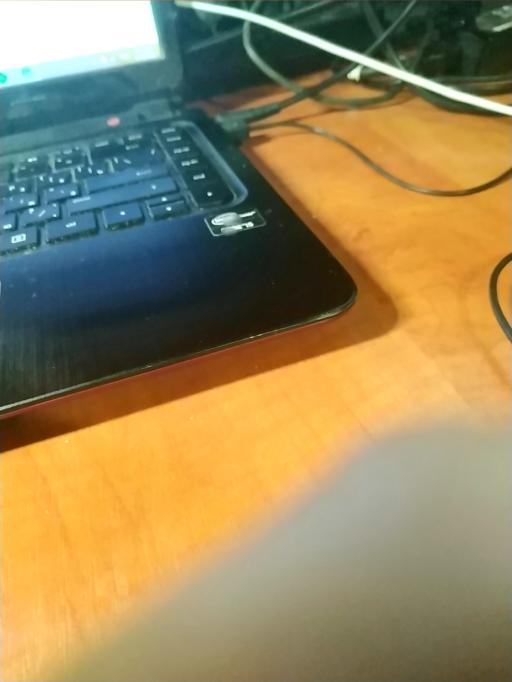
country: RU
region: Tverskaya
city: Vyshniy Volochek
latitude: 57.4024
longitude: 34.5171
